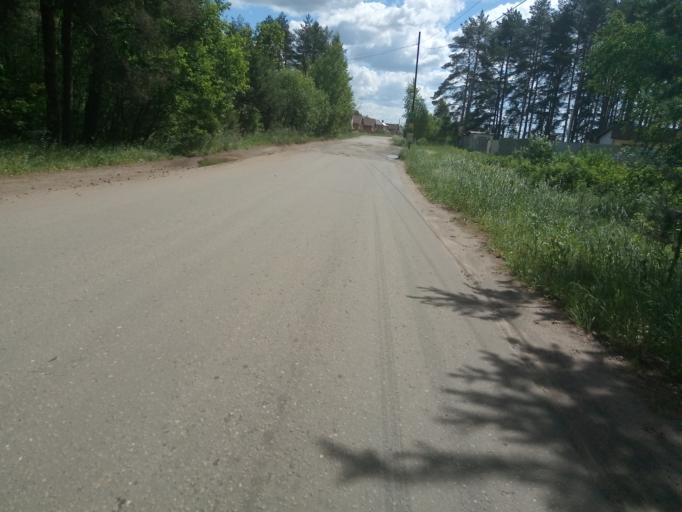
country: RU
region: Jaroslavl
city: Yaroslavl
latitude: 57.6546
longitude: 39.9854
